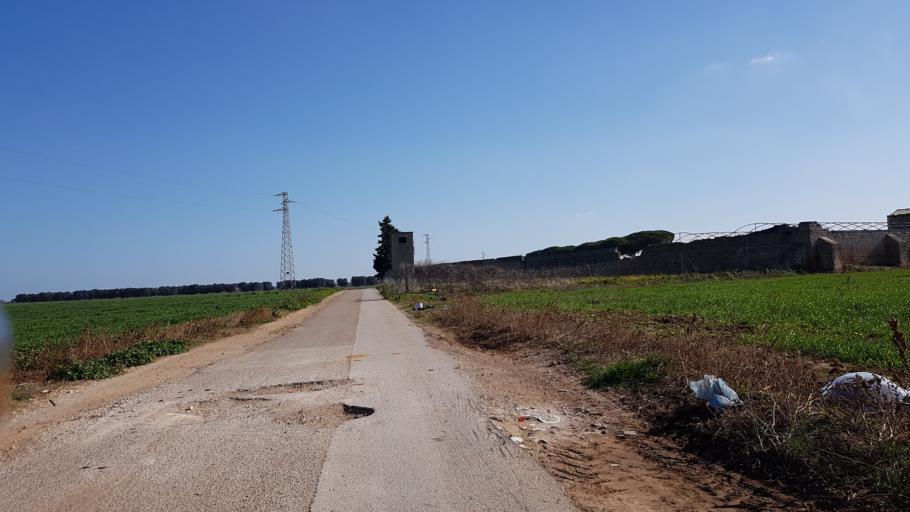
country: IT
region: Apulia
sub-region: Provincia di Brindisi
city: Mesagne
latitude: 40.6209
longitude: 17.8502
